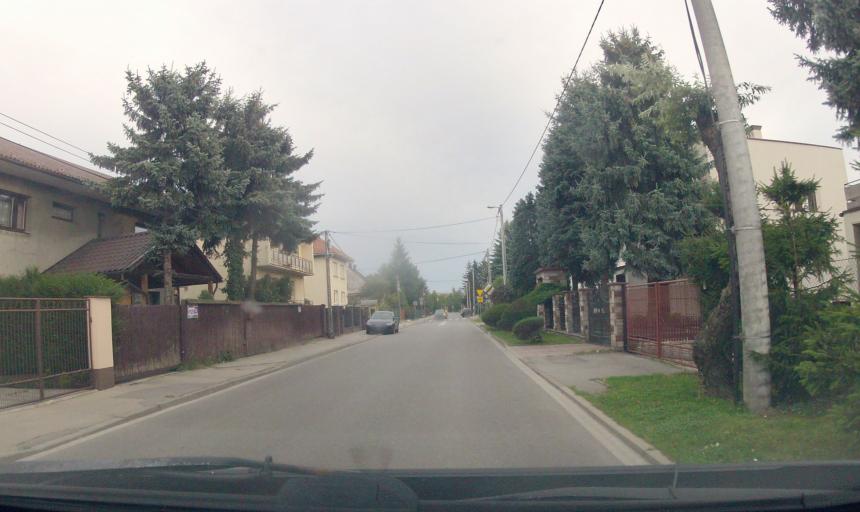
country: PL
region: Lesser Poland Voivodeship
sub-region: Krakow
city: Krakow
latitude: 50.0386
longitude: 19.9897
